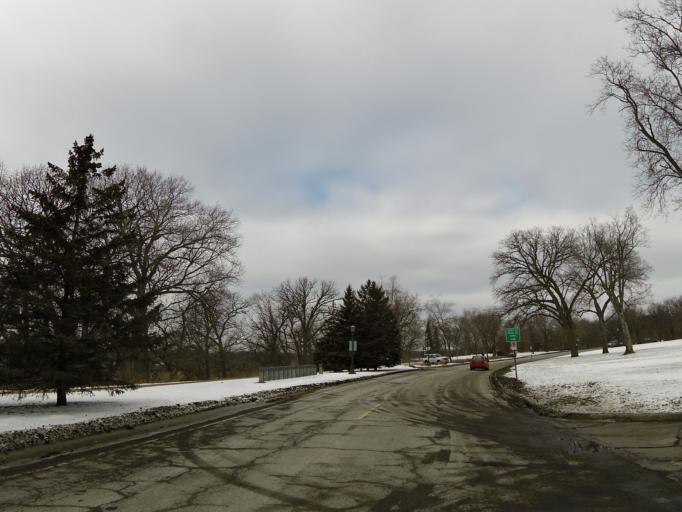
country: US
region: Minnesota
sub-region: Ramsey County
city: Lauderdale
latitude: 44.9400
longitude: -93.1978
